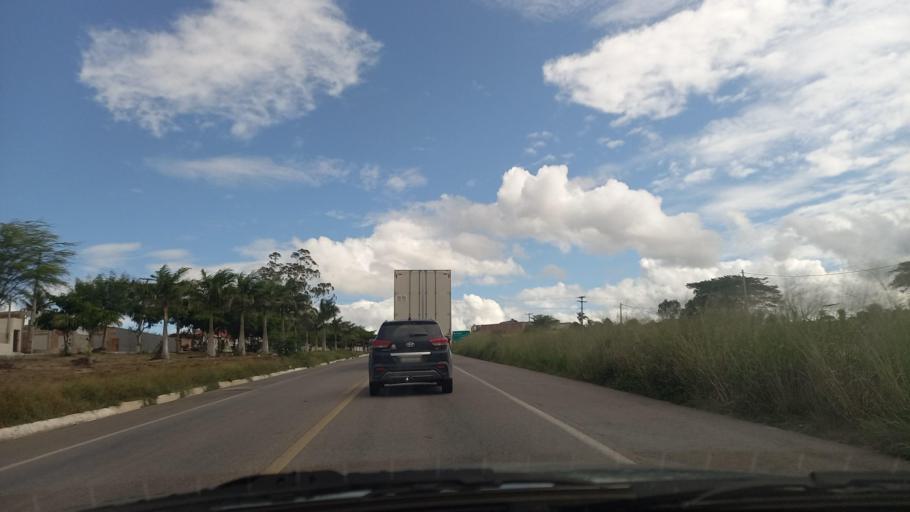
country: BR
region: Pernambuco
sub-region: Lajedo
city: Lajedo
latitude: -8.7065
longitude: -36.4178
